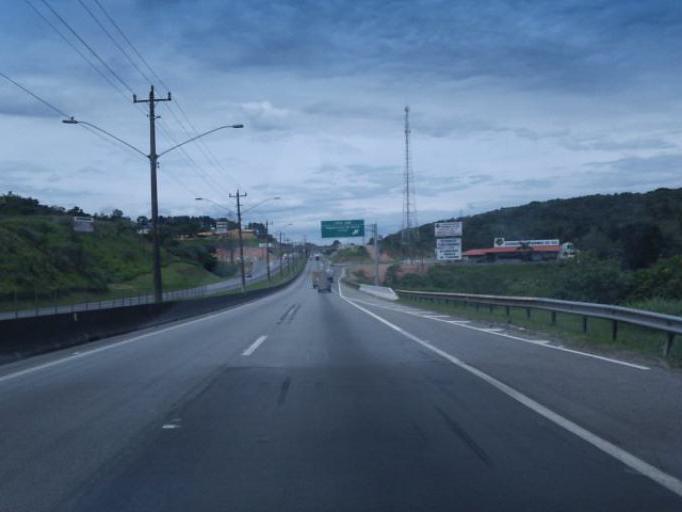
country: BR
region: Sao Paulo
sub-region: Itapecerica Da Serra
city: Itapecerica da Serra
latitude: -23.7039
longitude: -46.8728
